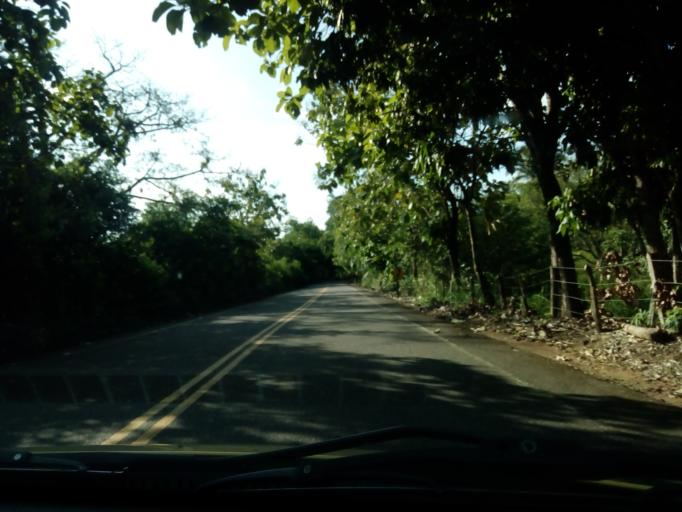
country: CO
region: Boyaca
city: Puerto Boyaca
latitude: 5.9351
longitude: -74.5407
